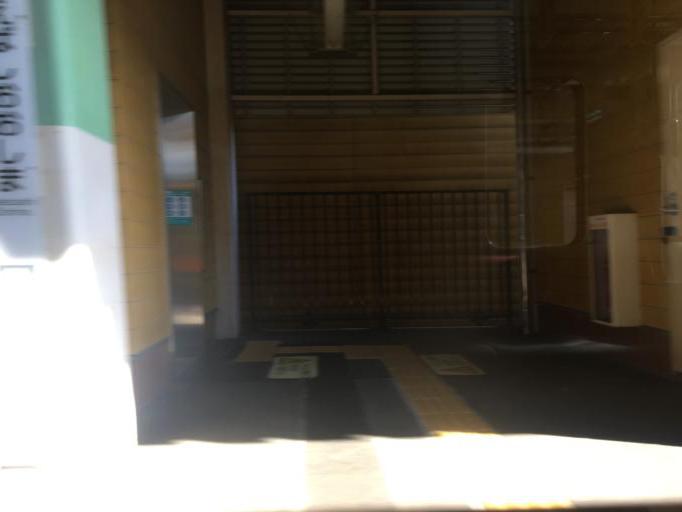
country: JP
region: Gunma
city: Maebashi-shi
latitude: 36.3706
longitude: 139.1097
